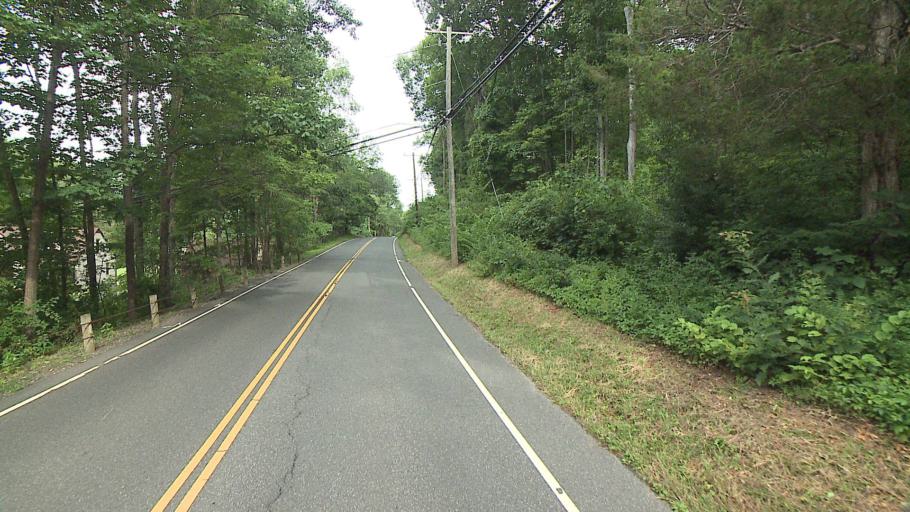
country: US
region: Connecticut
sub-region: Litchfield County
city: Woodbury
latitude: 41.5775
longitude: -73.2397
